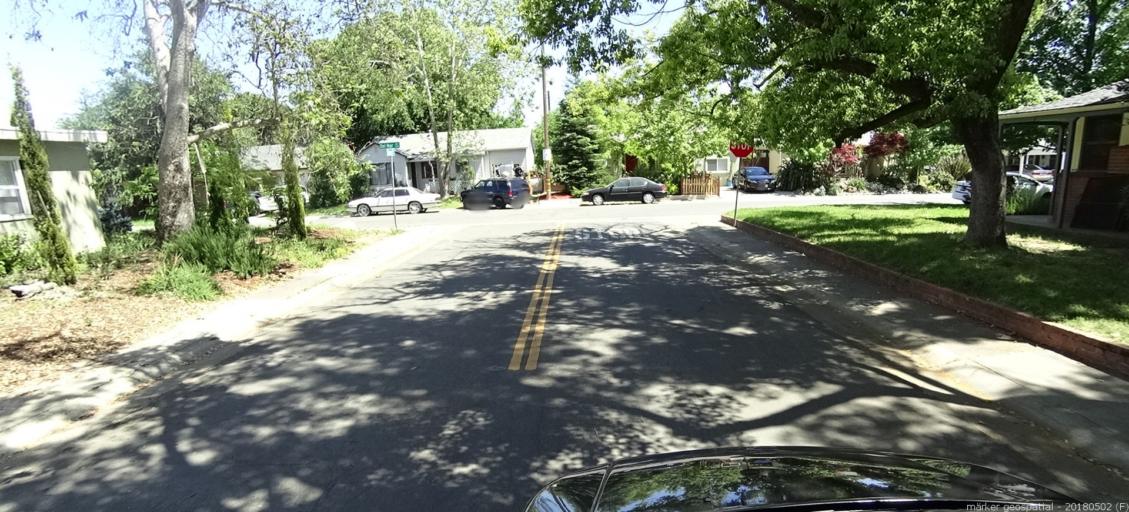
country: US
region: California
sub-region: Sacramento County
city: Arden-Arcade
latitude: 38.6272
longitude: -121.4353
